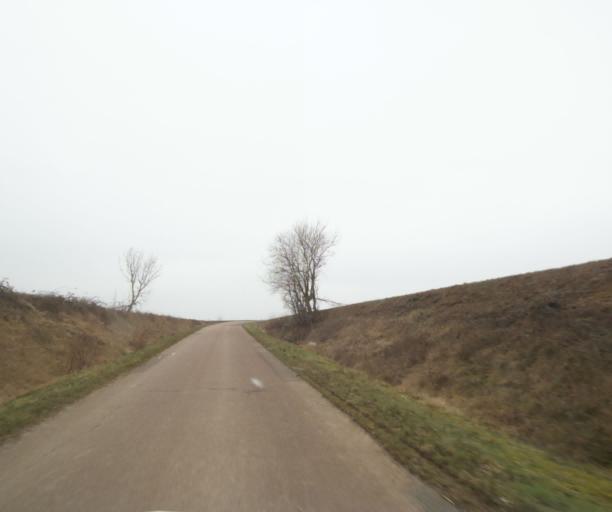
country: FR
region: Champagne-Ardenne
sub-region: Departement de la Haute-Marne
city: Chevillon
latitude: 48.5159
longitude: 5.0906
